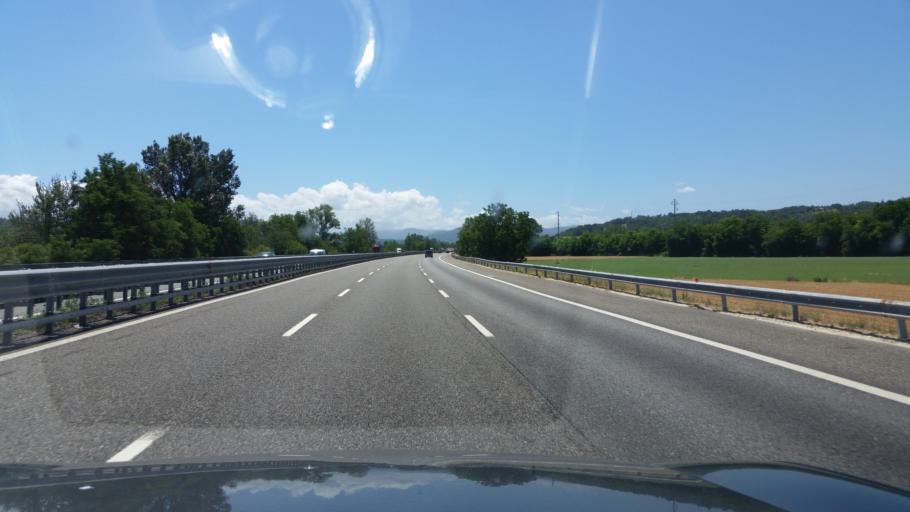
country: IT
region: Piedmont
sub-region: Provincia di Alessandria
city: Silvano d'Orba
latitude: 44.7050
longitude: 8.6675
